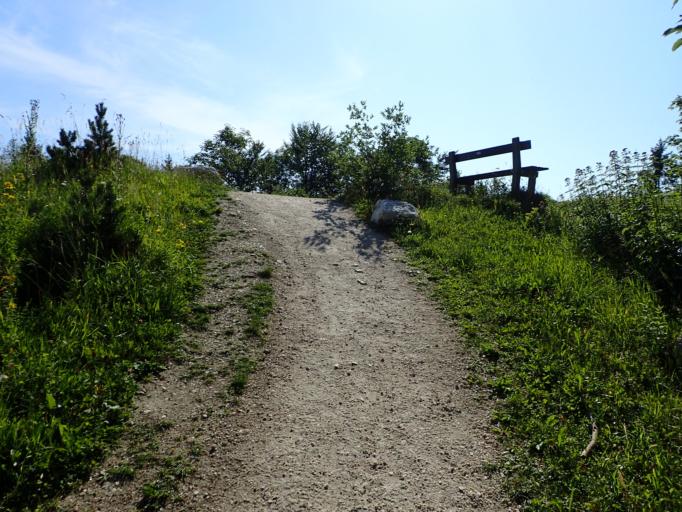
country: DE
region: Bavaria
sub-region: Upper Bavaria
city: Berchtesgaden
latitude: 47.6585
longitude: 13.0194
